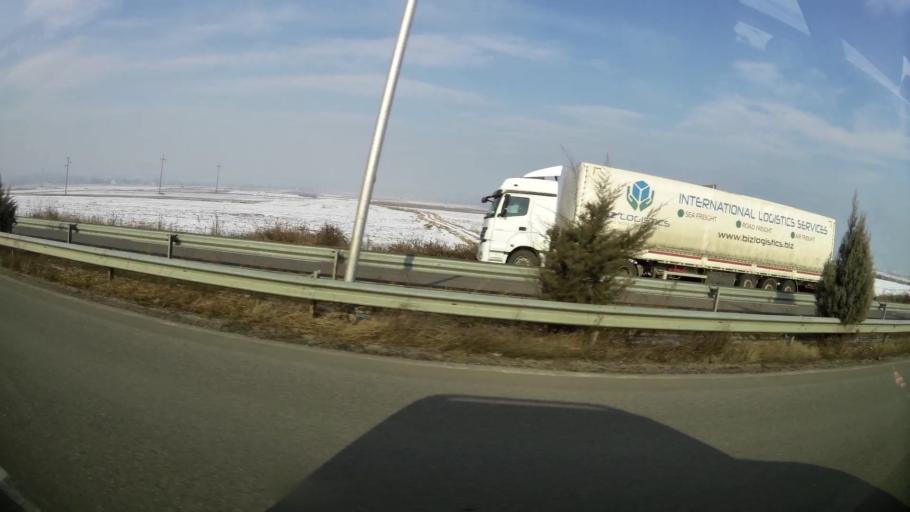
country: MK
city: Creshevo
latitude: 42.0306
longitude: 21.5061
